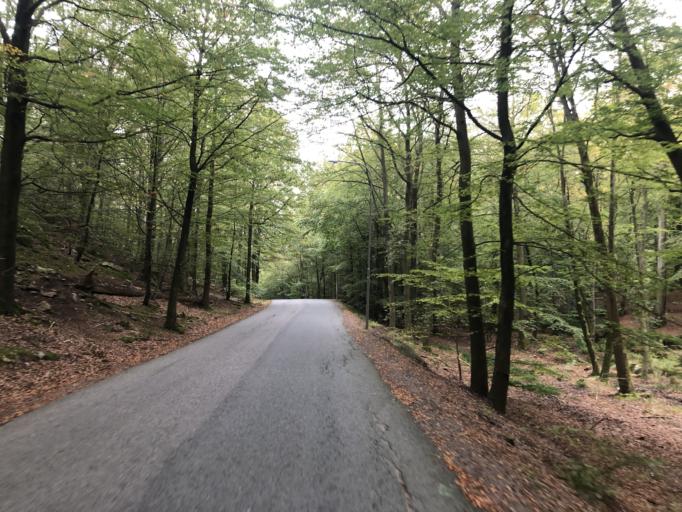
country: SE
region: Vaestra Goetaland
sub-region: Molndal
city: Moelndal
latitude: 57.6725
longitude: 12.0266
